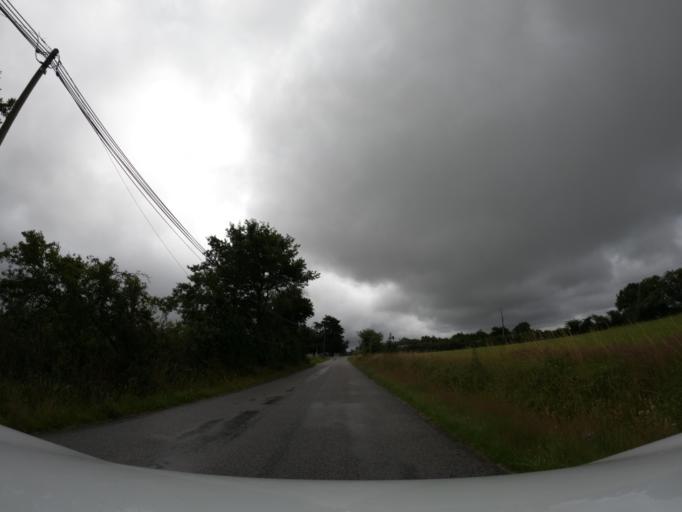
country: FR
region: Pays de la Loire
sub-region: Departement de la Loire-Atlantique
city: Saint-Mars-du-Desert
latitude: 47.3732
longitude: -1.4081
